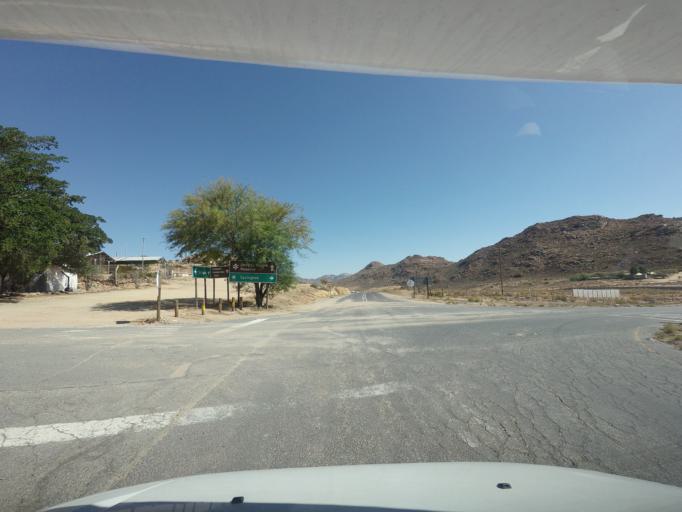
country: ZA
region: Northern Cape
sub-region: Namakwa District Municipality
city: Springbok
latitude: -29.6651
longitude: 17.8985
